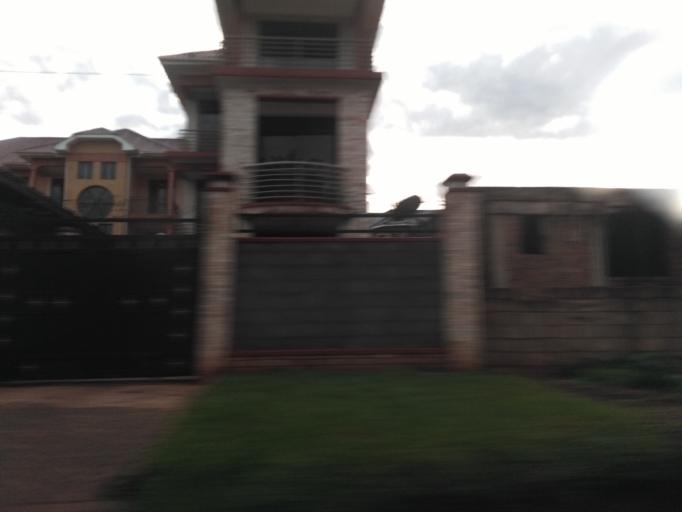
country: UG
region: Eastern Region
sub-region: Jinja District
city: Jinja
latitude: 0.4431
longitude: 33.2029
